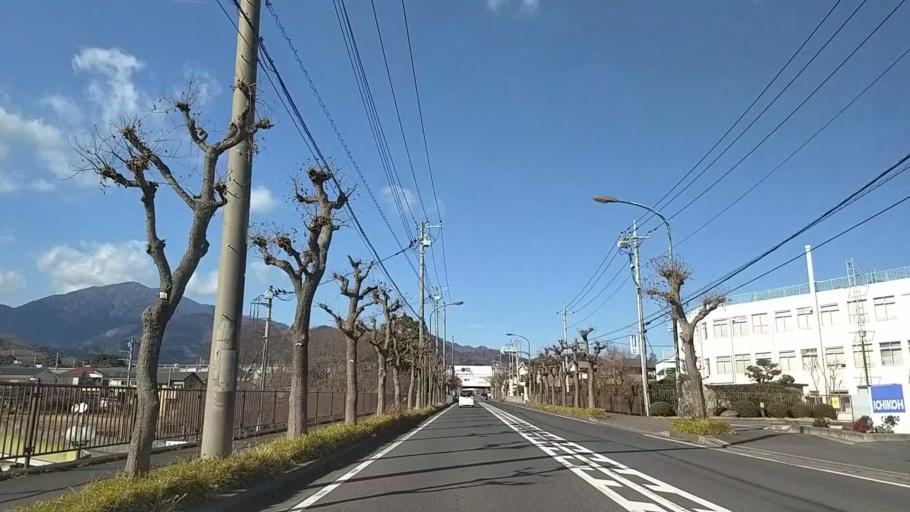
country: JP
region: Kanagawa
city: Isehara
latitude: 35.4033
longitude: 139.2960
